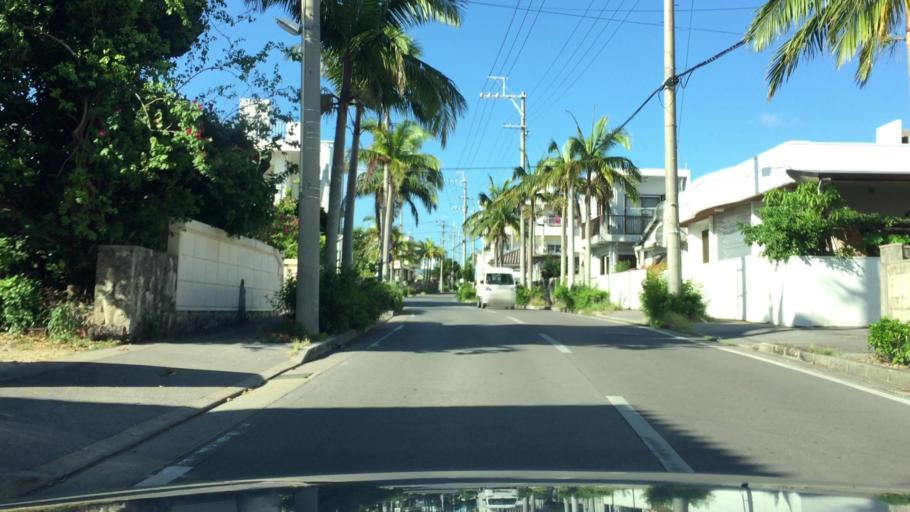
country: JP
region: Okinawa
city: Ishigaki
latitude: 24.3440
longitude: 124.1597
